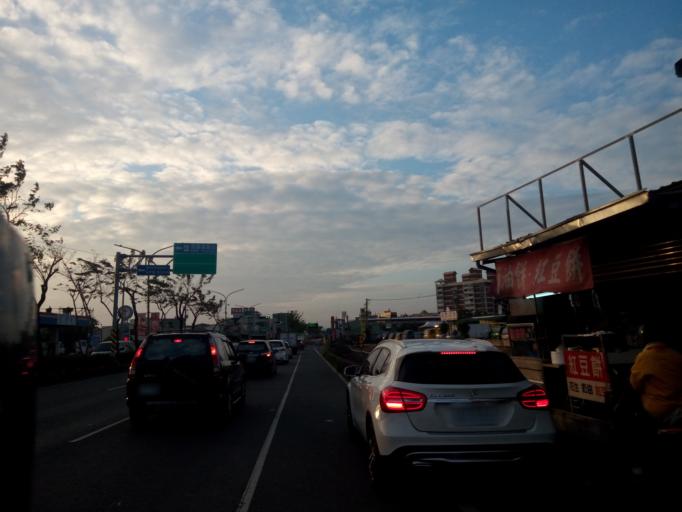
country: TW
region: Taiwan
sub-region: Chiayi
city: Jiayi Shi
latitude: 23.4918
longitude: 120.3990
